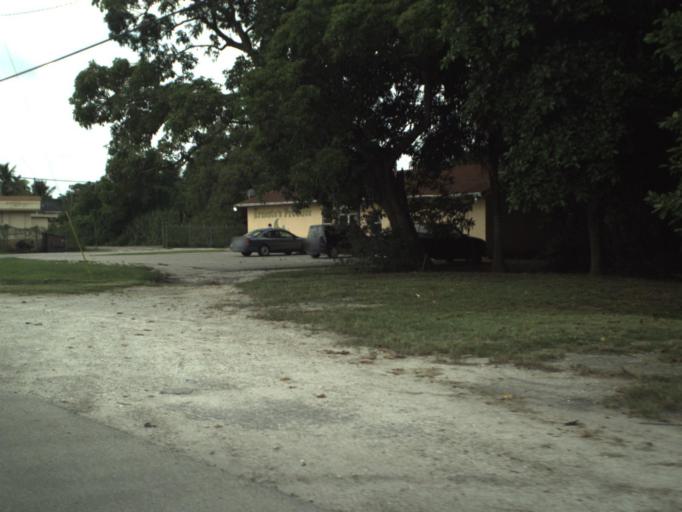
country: US
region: Florida
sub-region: Palm Beach County
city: Belle Glade
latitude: 26.6924
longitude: -80.6840
